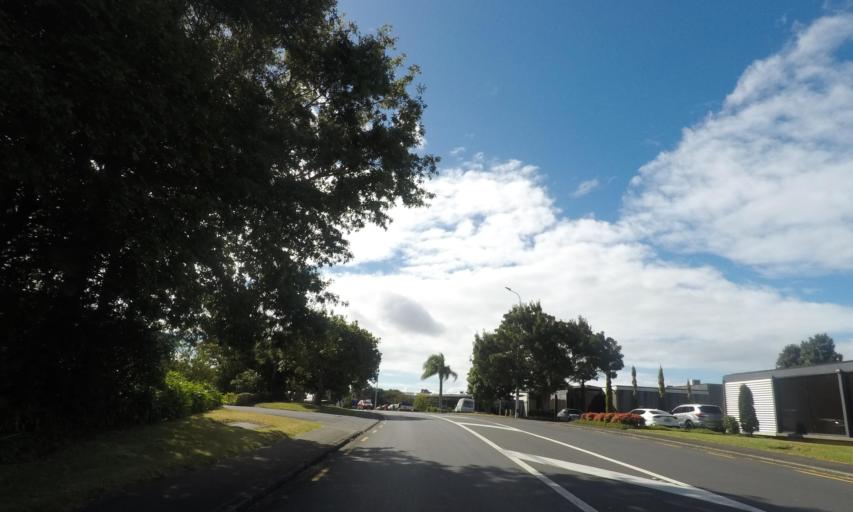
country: NZ
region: Auckland
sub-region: Auckland
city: Tamaki
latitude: -36.9240
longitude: 174.8519
